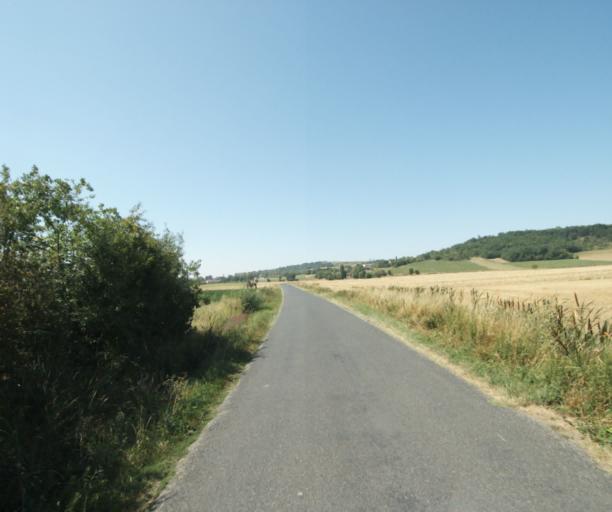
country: FR
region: Midi-Pyrenees
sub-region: Departement de la Haute-Garonne
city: Revel
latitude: 43.5141
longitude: 1.9564
